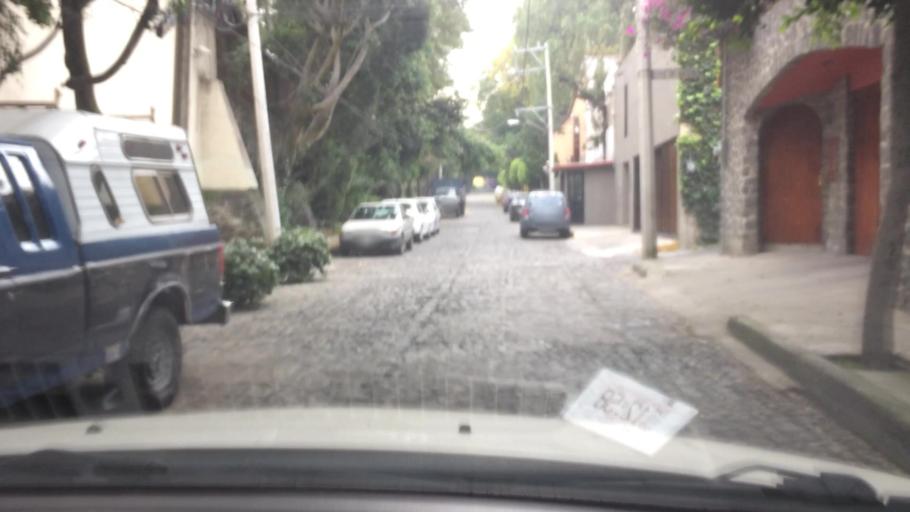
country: MX
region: Mexico City
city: Alvaro Obregon
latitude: 19.3539
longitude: -99.1975
